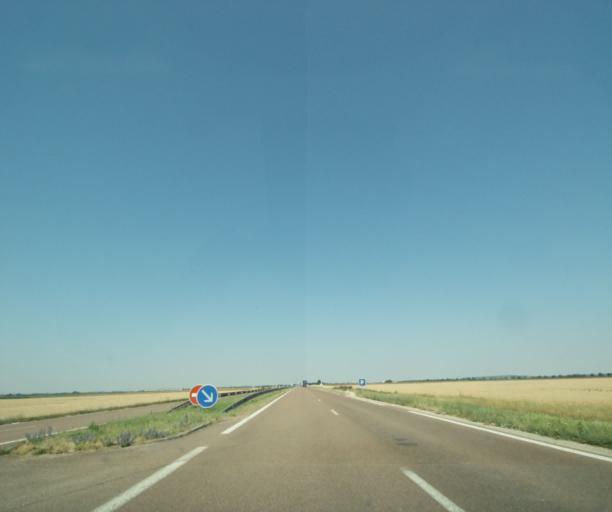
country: FR
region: Champagne-Ardenne
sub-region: Departement de la Marne
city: Frignicourt
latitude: 48.6963
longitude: 4.6936
